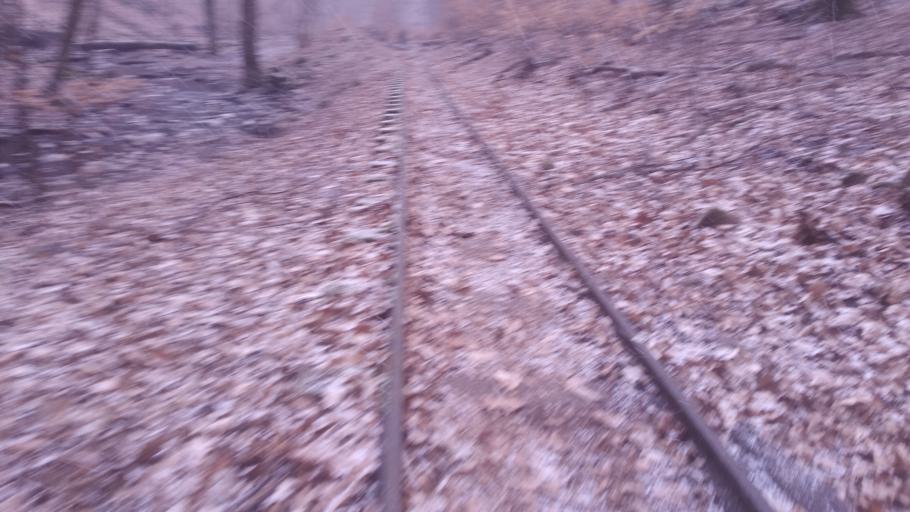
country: SK
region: Nitriansky
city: Sahy
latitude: 47.9589
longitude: 18.9020
